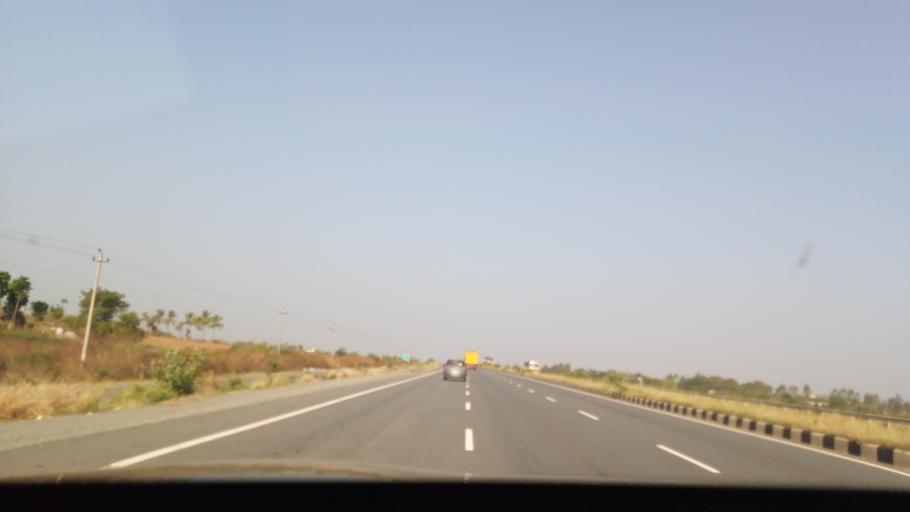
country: IN
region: Karnataka
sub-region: Haveri
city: Ranibennur
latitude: 14.5890
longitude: 75.6563
